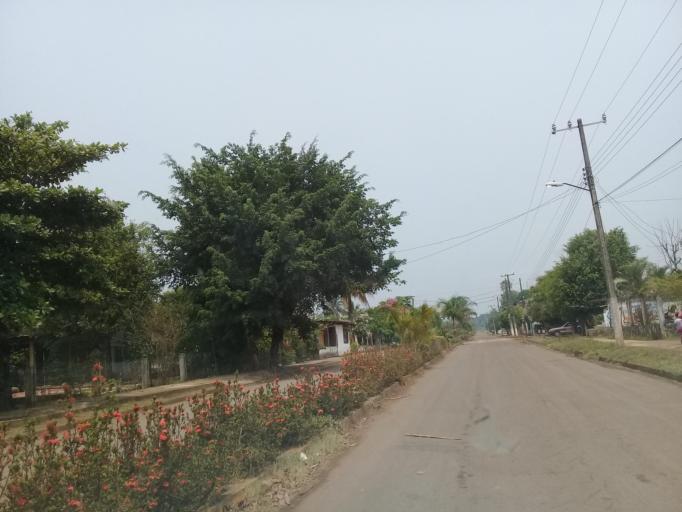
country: MX
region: Veracruz
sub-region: Tezonapa
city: Laguna Chica (Pueblo Nuevo)
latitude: 18.5163
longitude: -96.7193
